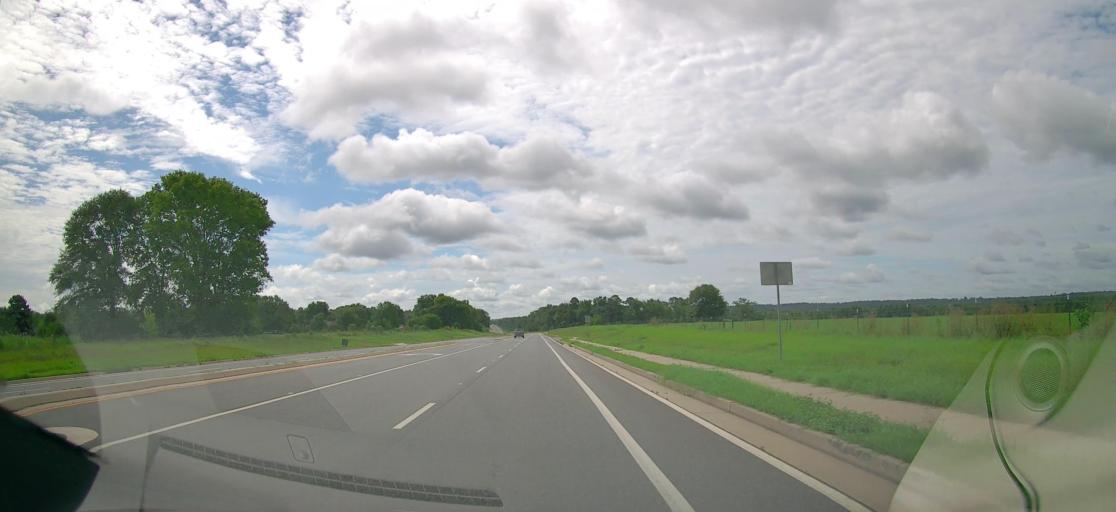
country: US
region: Georgia
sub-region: Houston County
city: Centerville
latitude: 32.6987
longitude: -83.6927
